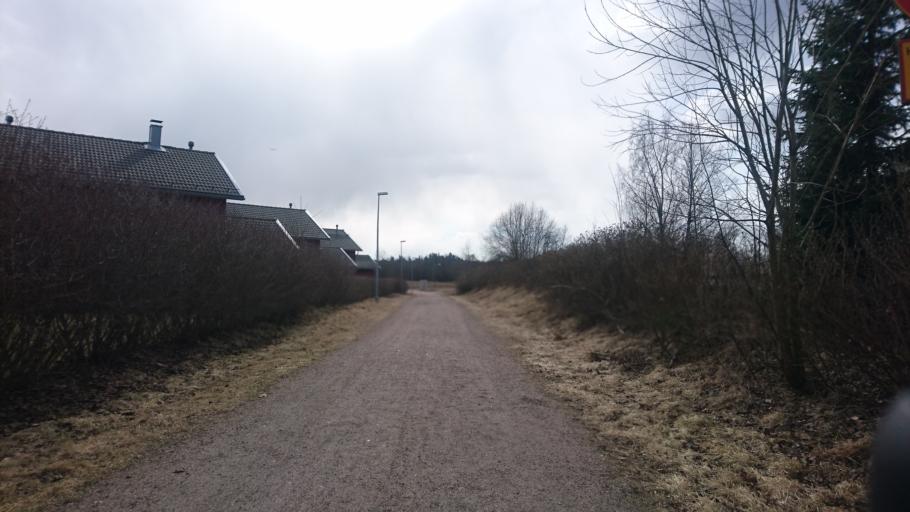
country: FI
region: Uusimaa
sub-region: Helsinki
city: Espoo
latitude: 60.2190
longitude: 24.6698
